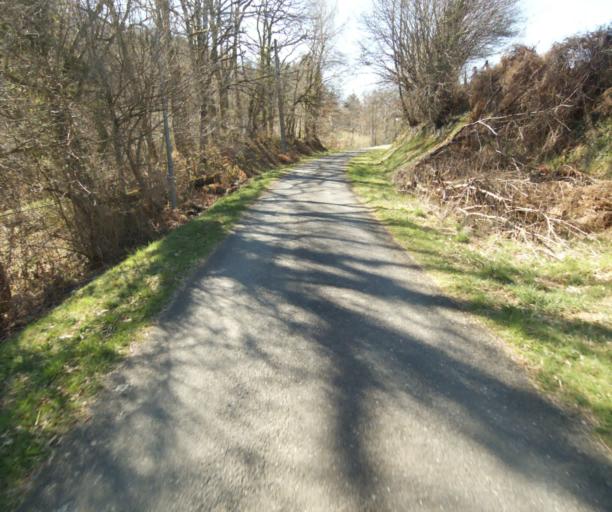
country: FR
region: Limousin
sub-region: Departement de la Correze
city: Saint-Clement
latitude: 45.3460
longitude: 1.6718
